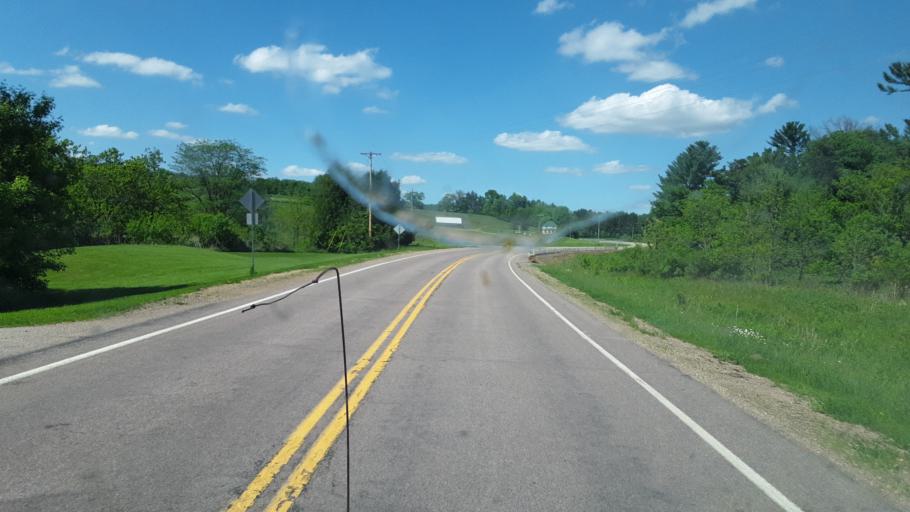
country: US
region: Wisconsin
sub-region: Richland County
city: Richland Center
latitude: 43.4254
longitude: -90.2431
